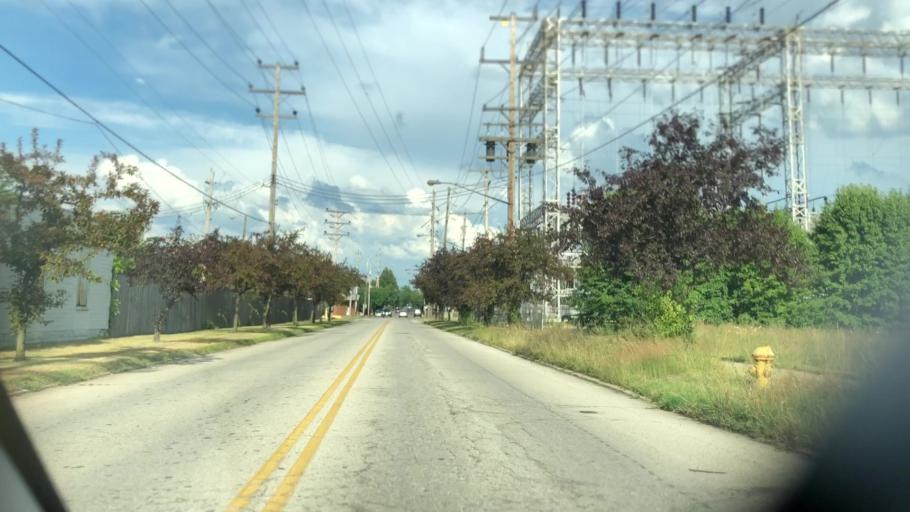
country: US
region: Ohio
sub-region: Summit County
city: Barberton
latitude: 41.0178
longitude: -81.6167
